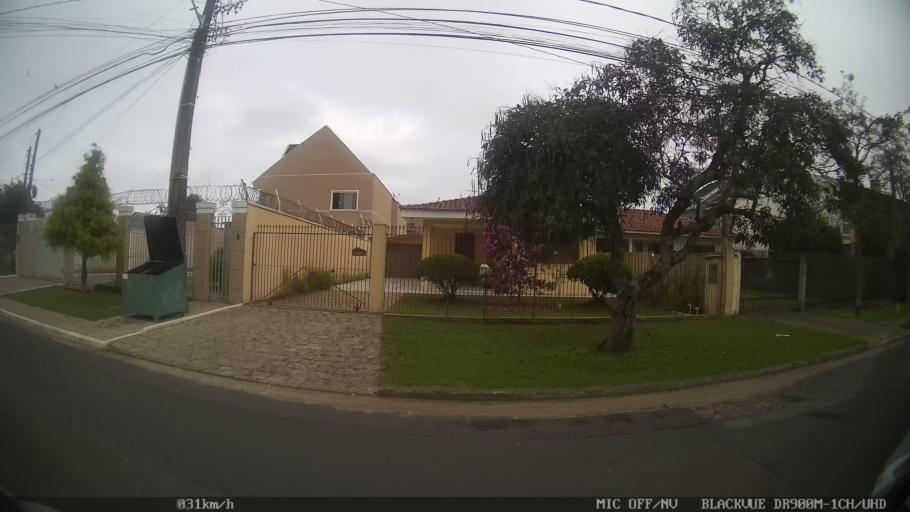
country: BR
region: Parana
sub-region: Almirante Tamandare
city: Almirante Tamandare
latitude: -25.3814
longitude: -49.3256
